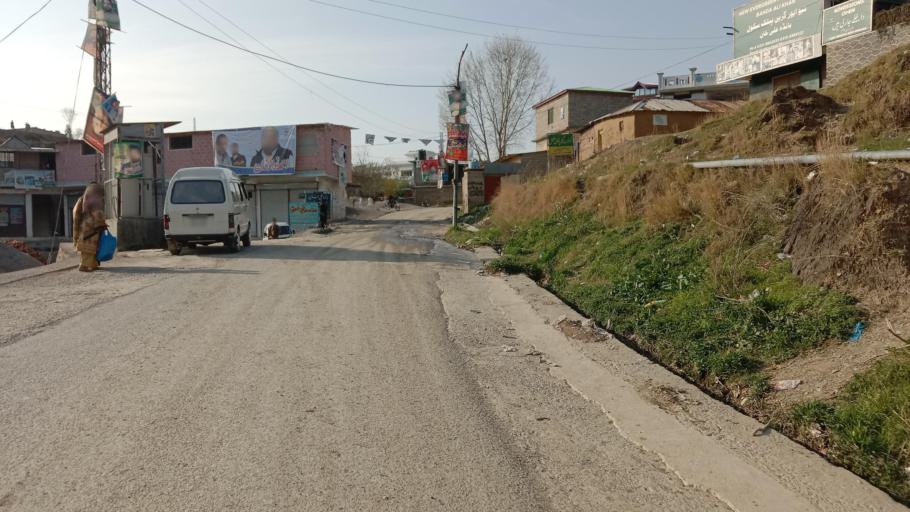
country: PK
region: Khyber Pakhtunkhwa
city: Abbottabad
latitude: 34.2038
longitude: 73.2201
